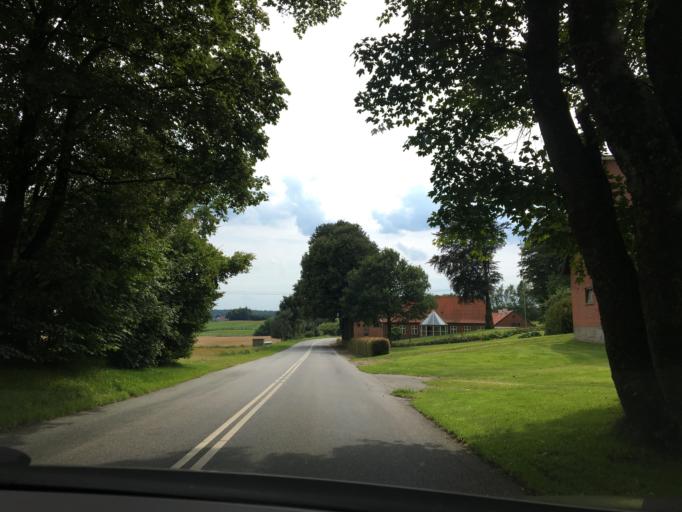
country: DK
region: Central Jutland
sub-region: Viborg Kommune
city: Stoholm
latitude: 56.4737
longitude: 9.1474
